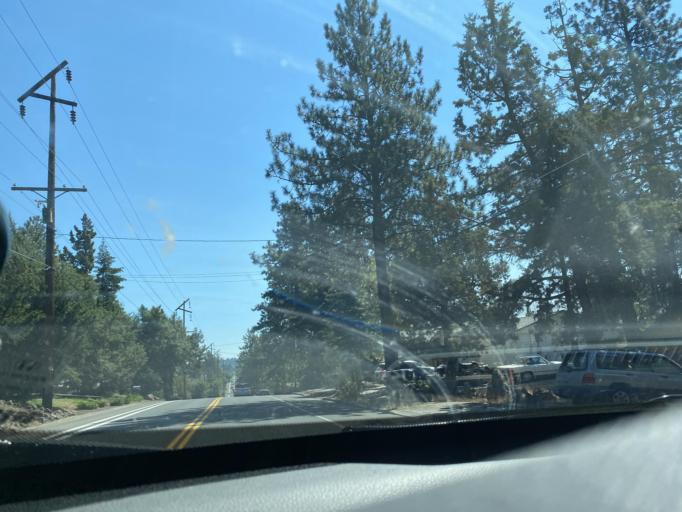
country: US
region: Oregon
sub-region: Deschutes County
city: Bend
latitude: 44.0641
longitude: -121.3311
